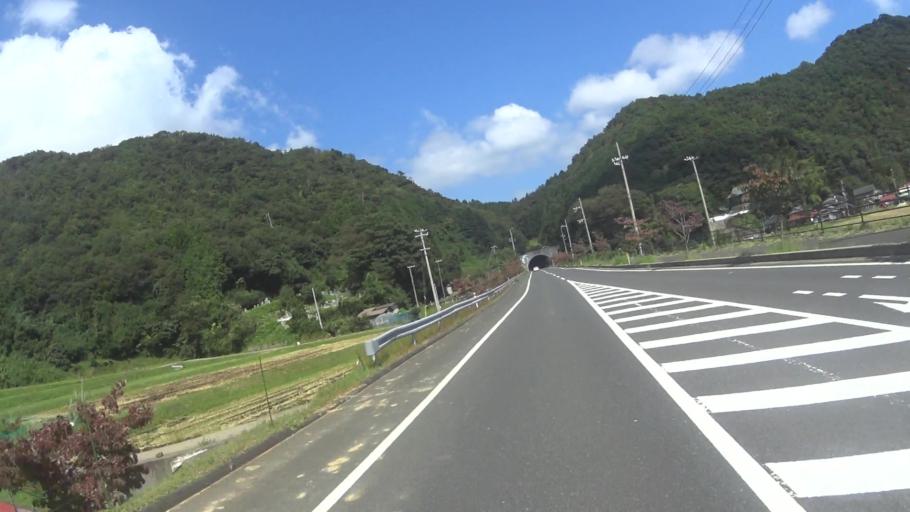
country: JP
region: Kyoto
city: Miyazu
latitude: 35.6679
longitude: 135.2667
